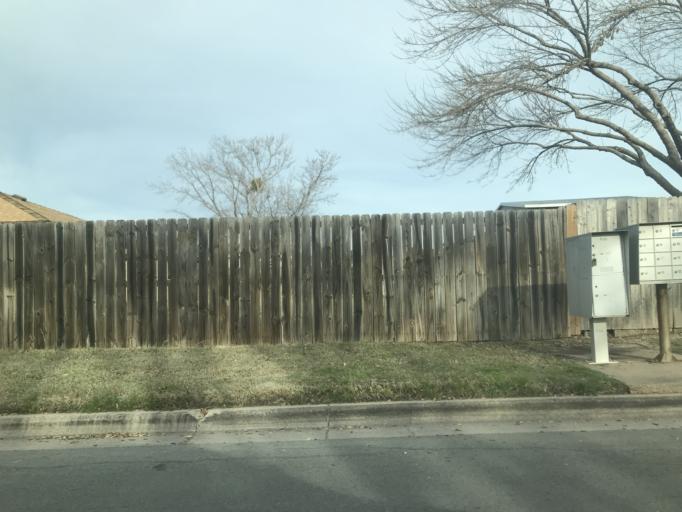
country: US
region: Texas
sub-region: Taylor County
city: Abilene
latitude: 32.3993
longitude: -99.7691
